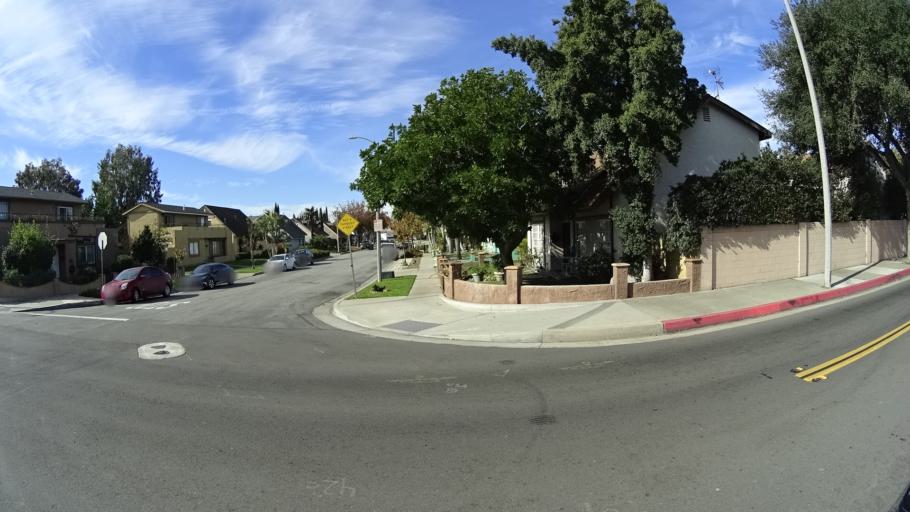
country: US
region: California
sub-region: Orange County
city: Santa Ana
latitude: 33.7617
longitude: -117.8560
